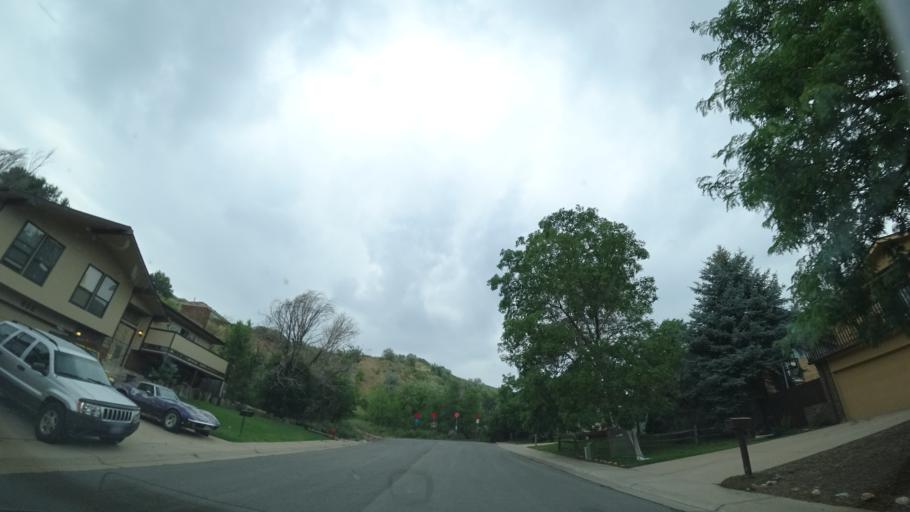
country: US
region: Colorado
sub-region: Jefferson County
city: West Pleasant View
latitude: 39.7005
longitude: -105.1551
